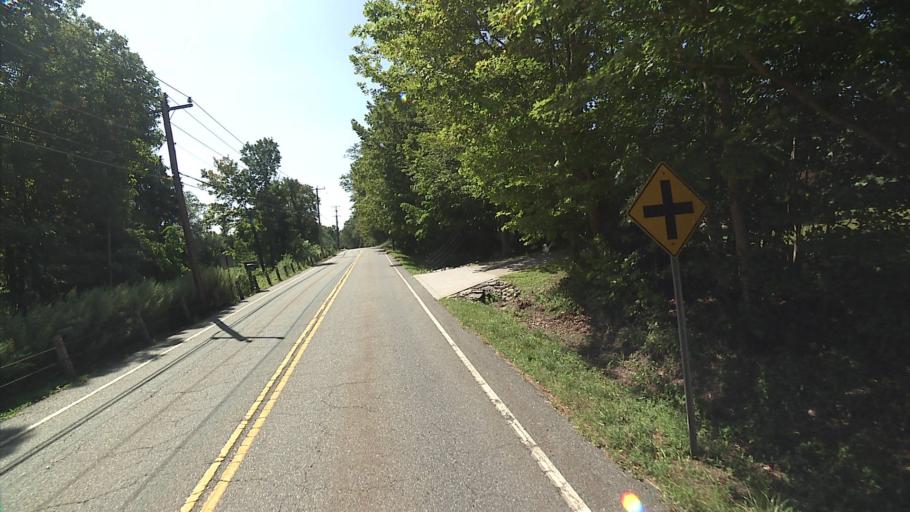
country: US
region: Connecticut
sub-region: Litchfield County
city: Northwest Harwinton
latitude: 41.7547
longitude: -73.0823
